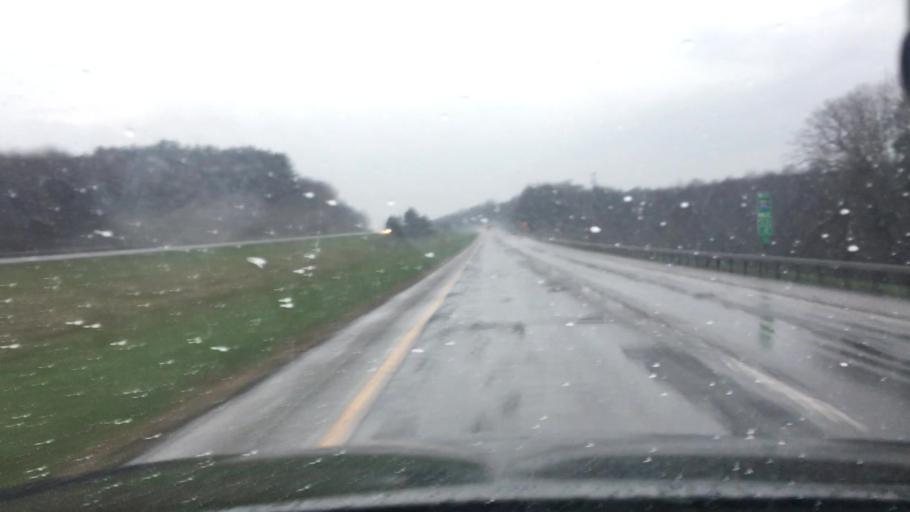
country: US
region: New York
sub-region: Chautauqua County
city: Lakewood
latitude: 42.1317
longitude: -79.3270
